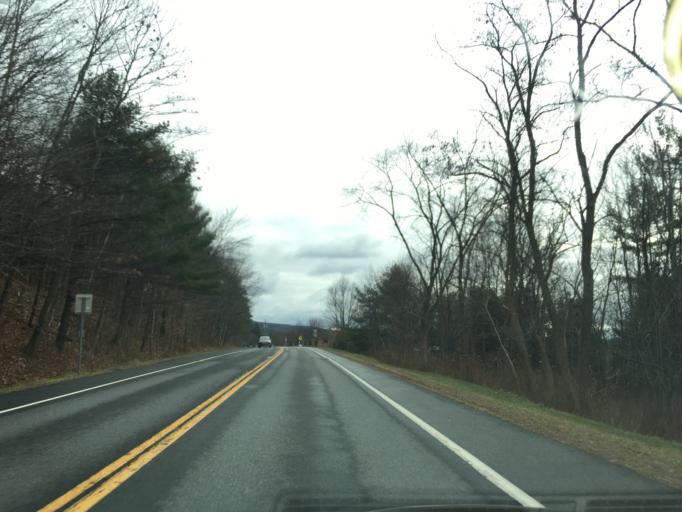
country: US
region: New York
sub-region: Rensselaer County
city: Averill Park
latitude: 42.6402
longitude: -73.5453
